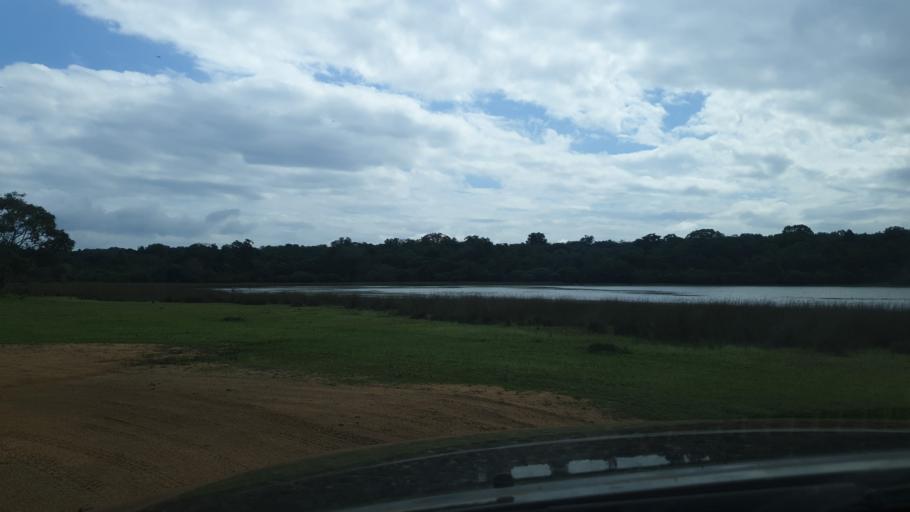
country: LK
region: North Central
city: Anuradhapura
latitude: 8.4257
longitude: 80.0226
